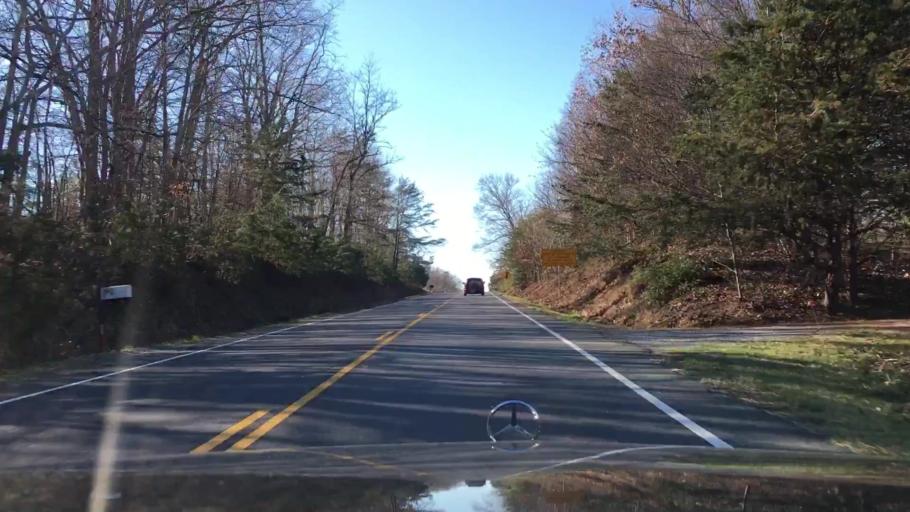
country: US
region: Virginia
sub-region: City of Bedford
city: Bedford
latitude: 37.2406
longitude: -79.6152
